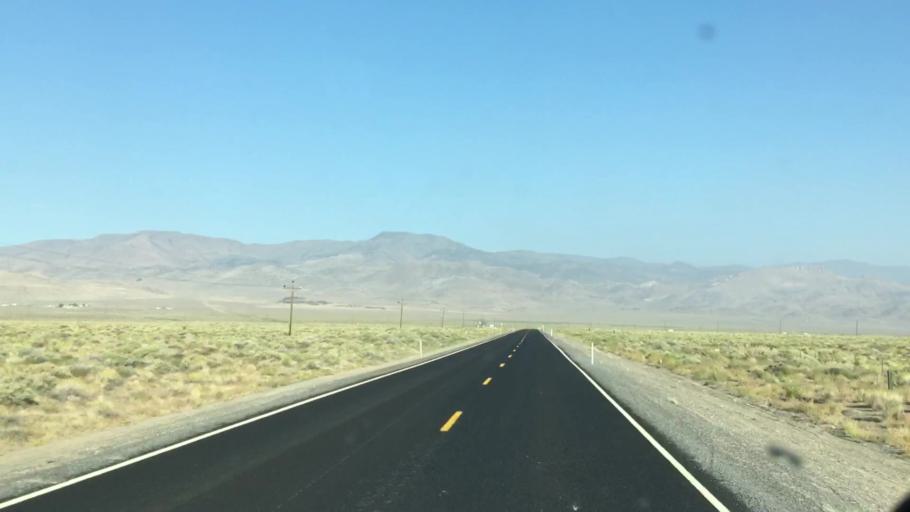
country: US
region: Nevada
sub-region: Lyon County
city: Fernley
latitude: 39.6477
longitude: -119.3166
